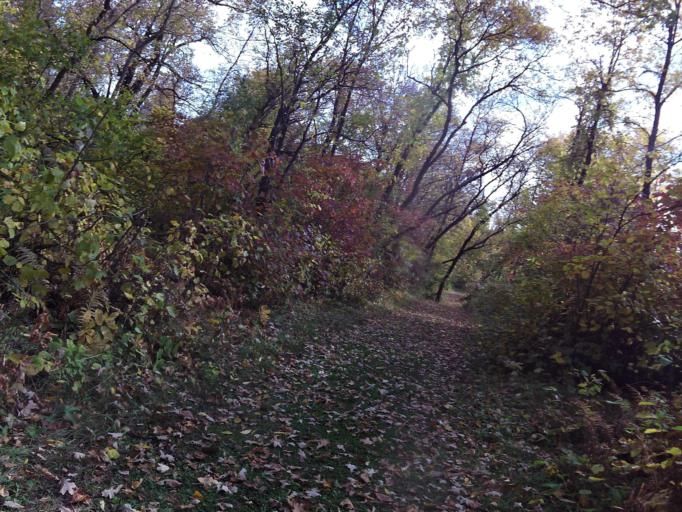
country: US
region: North Dakota
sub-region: Pembina County
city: Cavalier
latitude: 48.7774
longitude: -97.7385
